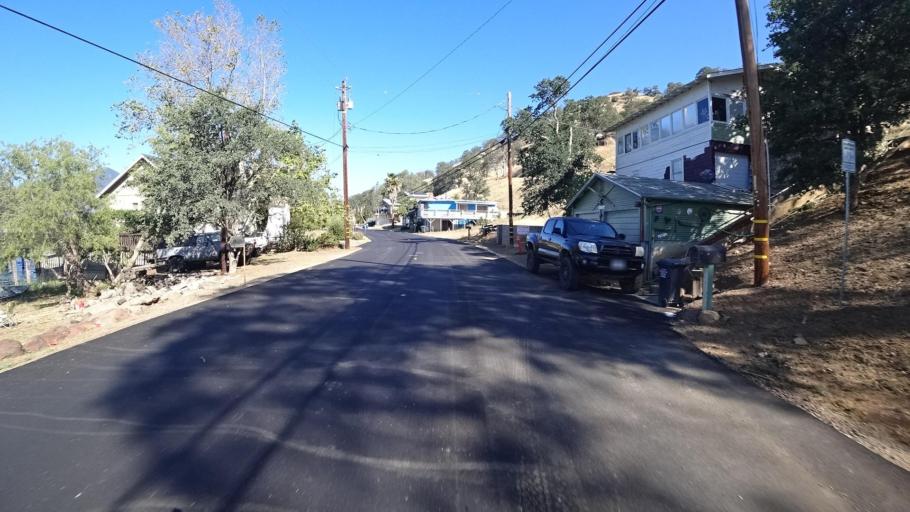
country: US
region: California
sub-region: Lake County
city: Clearlake
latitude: 38.9739
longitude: -122.6743
